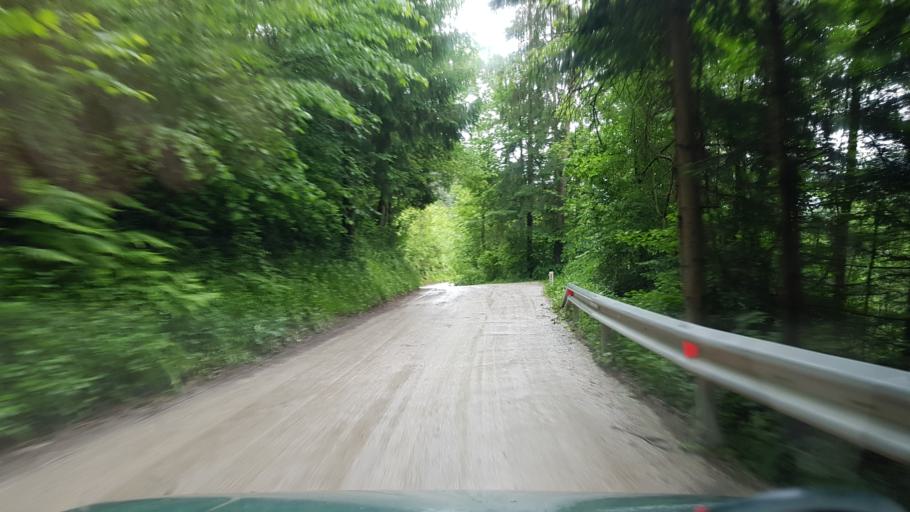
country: SI
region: Bled
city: Zasip
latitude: 46.3883
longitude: 14.1257
